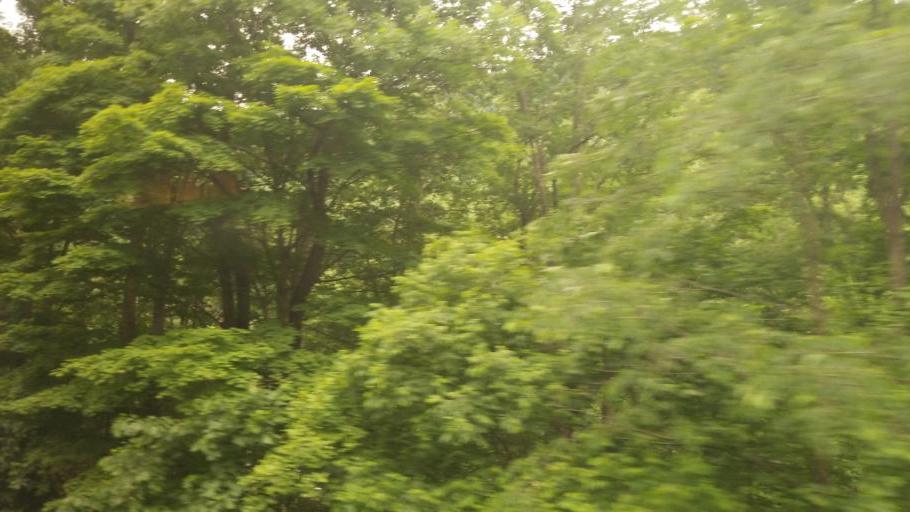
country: US
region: Pennsylvania
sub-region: Fayette County
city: South Connellsville
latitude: 39.8950
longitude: -79.4771
